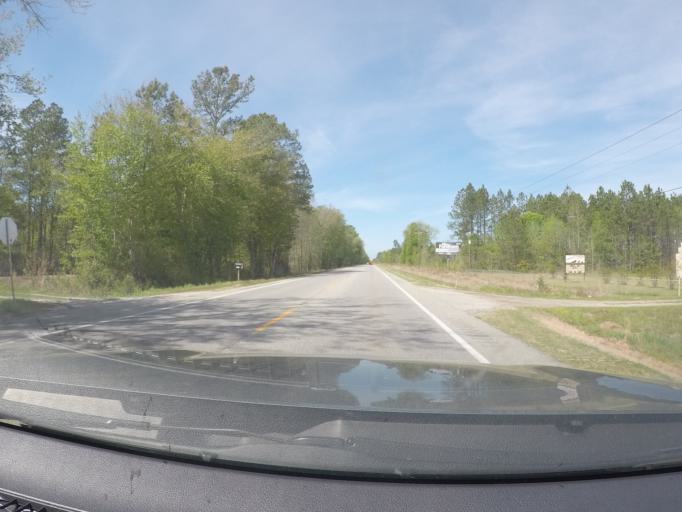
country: US
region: Georgia
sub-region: Bryan County
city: Pembroke
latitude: 32.1335
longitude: -81.5892
